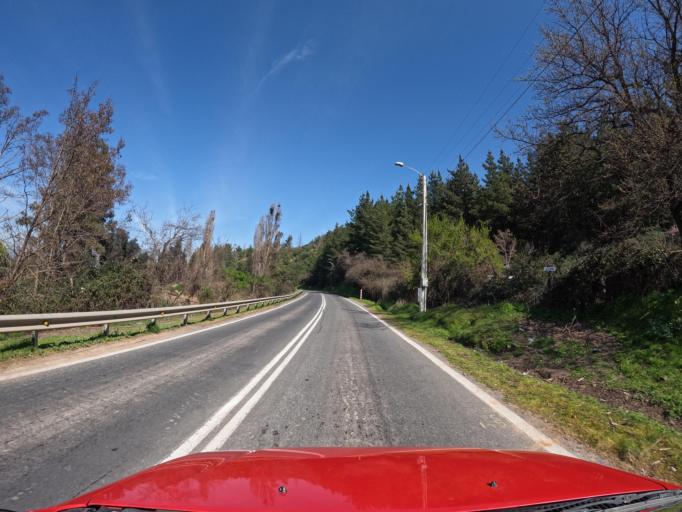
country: CL
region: Maule
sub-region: Provincia de Curico
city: Rauco
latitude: -34.9899
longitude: -71.4393
